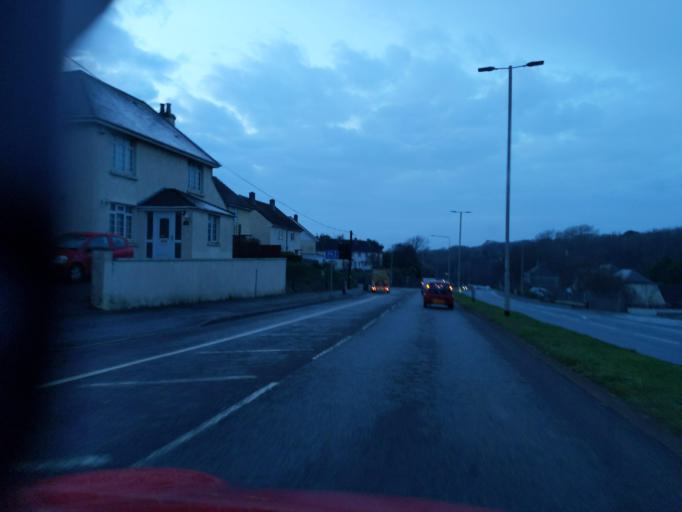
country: GB
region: England
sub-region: Plymouth
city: Plymstock
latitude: 50.3642
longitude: -4.0776
